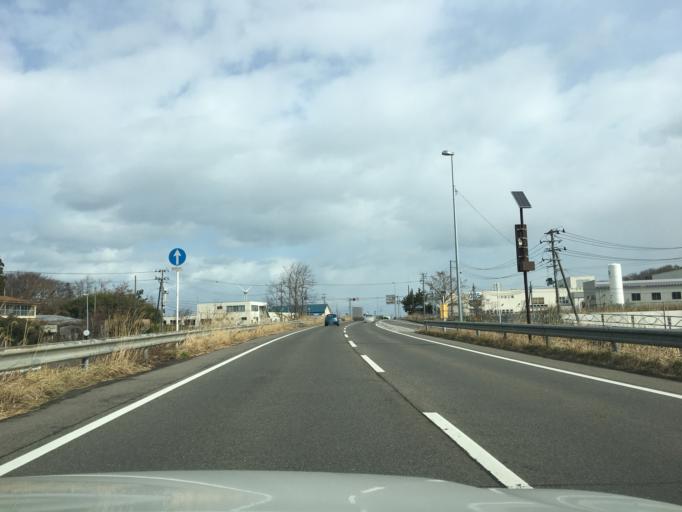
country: JP
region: Yamagata
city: Yuza
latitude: 39.2668
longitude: 139.9228
